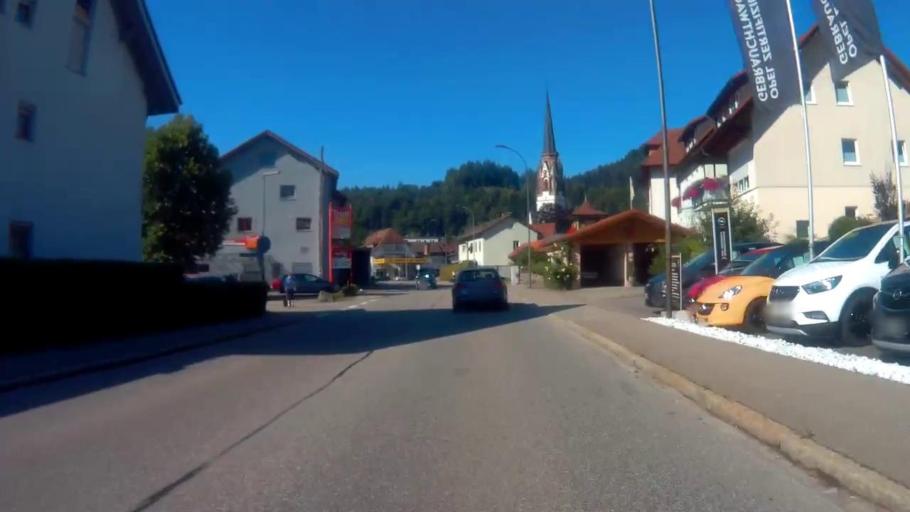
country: DE
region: Baden-Wuerttemberg
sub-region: Freiburg Region
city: Schonau im Schwarzwald
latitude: 47.7882
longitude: 7.8959
